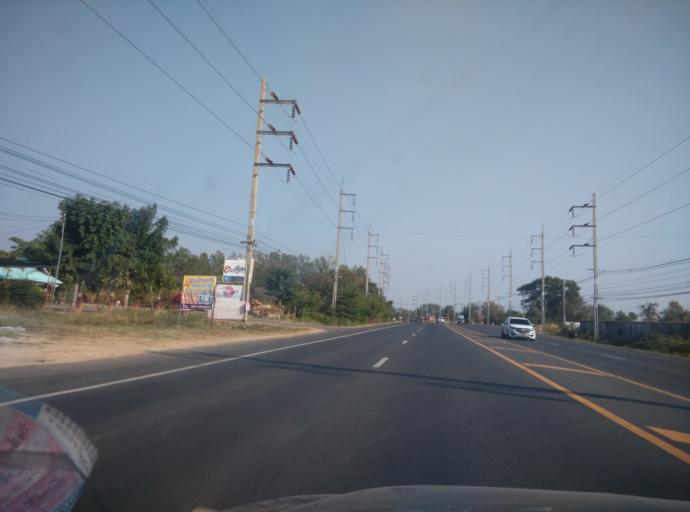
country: TH
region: Sisaket
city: Uthumphon Phisai
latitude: 15.1629
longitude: 104.1645
